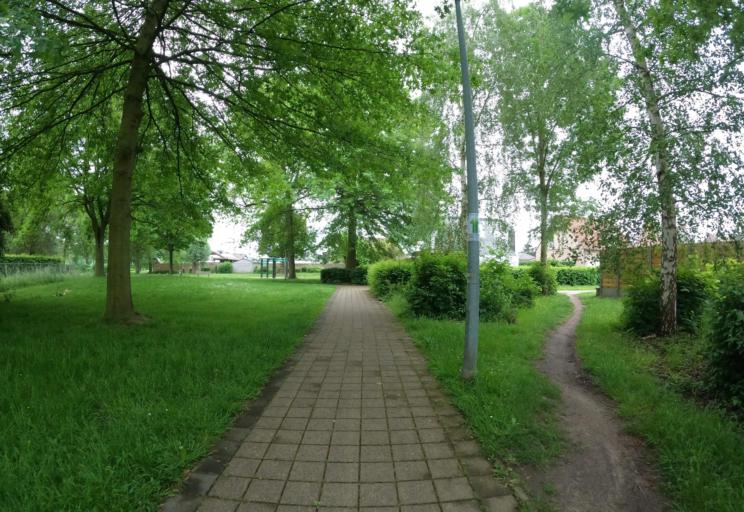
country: BE
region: Flanders
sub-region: Provincie Oost-Vlaanderen
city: Dendermonde
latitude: 51.0529
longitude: 4.1021
